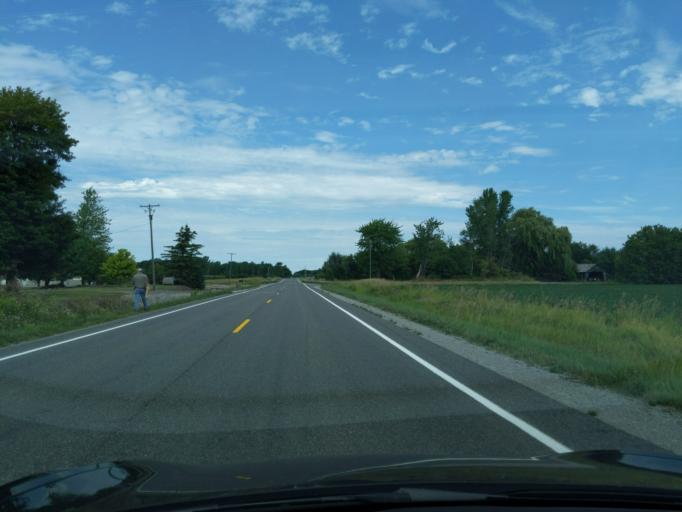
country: US
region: Michigan
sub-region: Gratiot County
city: Breckenridge
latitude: 43.5061
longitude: -84.3698
